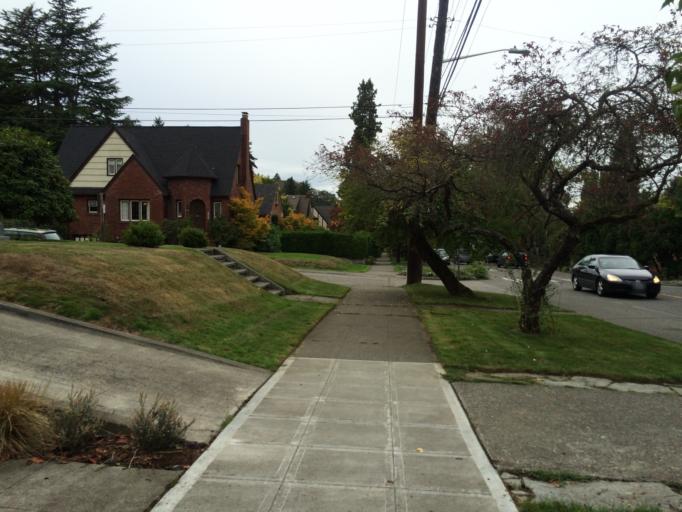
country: US
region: Washington
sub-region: King County
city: Seattle
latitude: 47.6369
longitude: -122.3051
